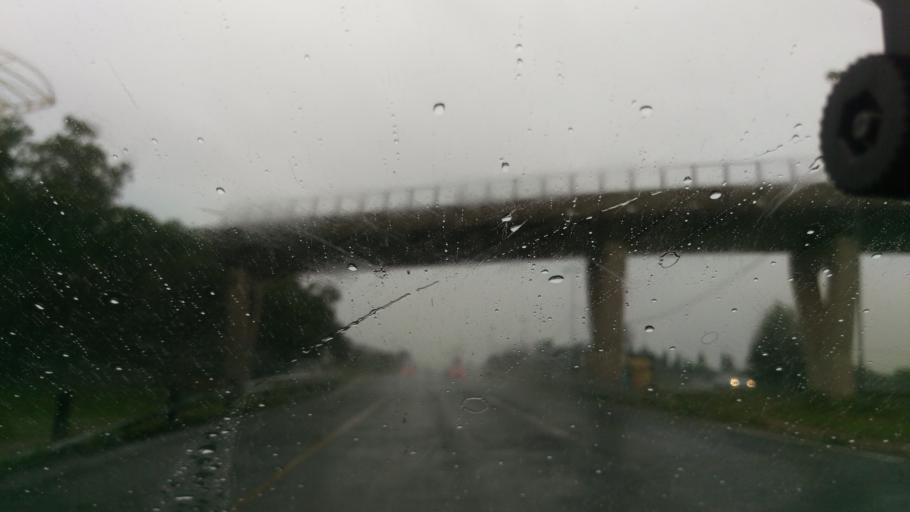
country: ZA
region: Gauteng
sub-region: West Rand District Municipality
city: Muldersdriseloop
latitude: -26.0620
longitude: 27.9424
